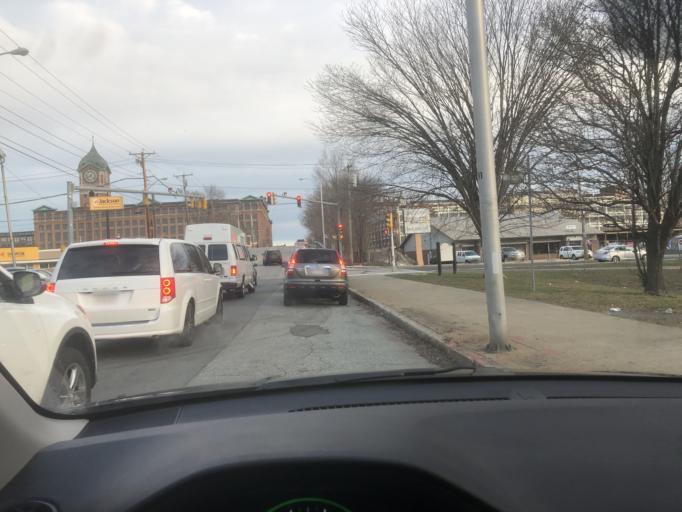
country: US
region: Massachusetts
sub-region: Essex County
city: Lawrence
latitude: 42.7003
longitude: -71.1534
